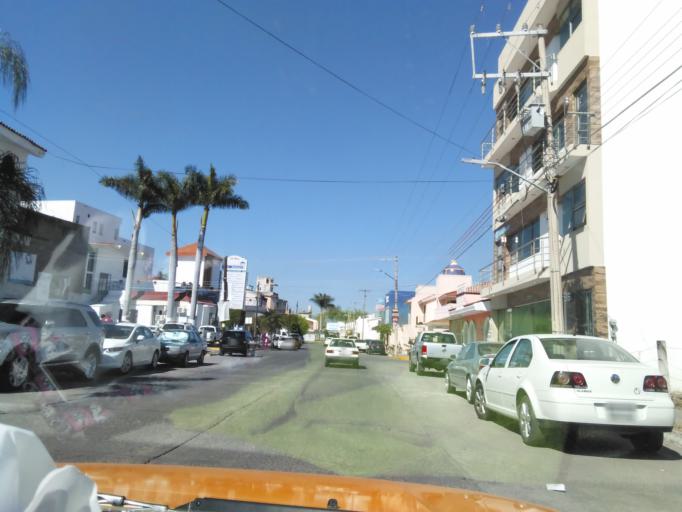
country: MX
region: Nayarit
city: Tepic
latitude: 21.4928
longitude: -104.8863
